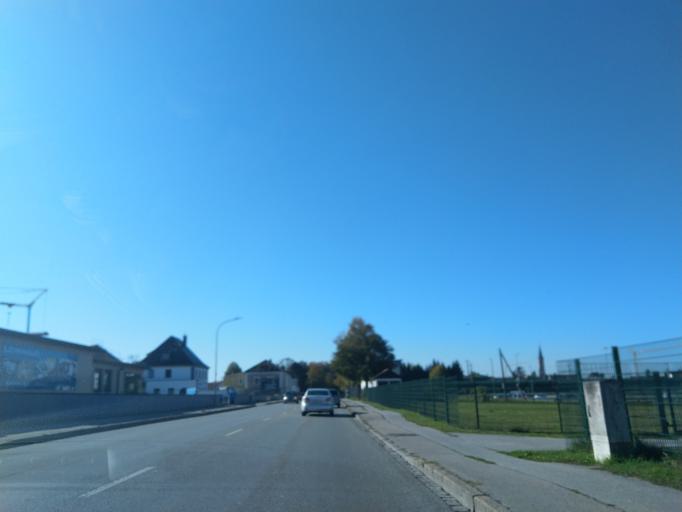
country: DE
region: Bavaria
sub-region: Lower Bavaria
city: Plattling
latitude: 48.7803
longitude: 12.8787
